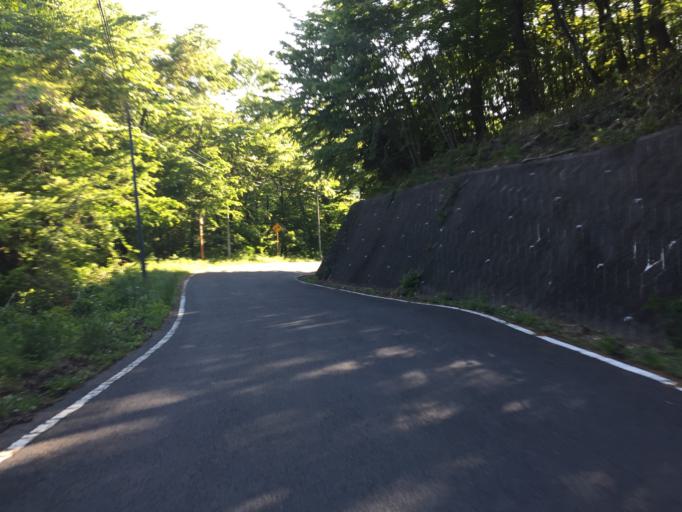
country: JP
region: Ibaraki
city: Kitaibaraki
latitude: 36.9041
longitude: 140.5915
